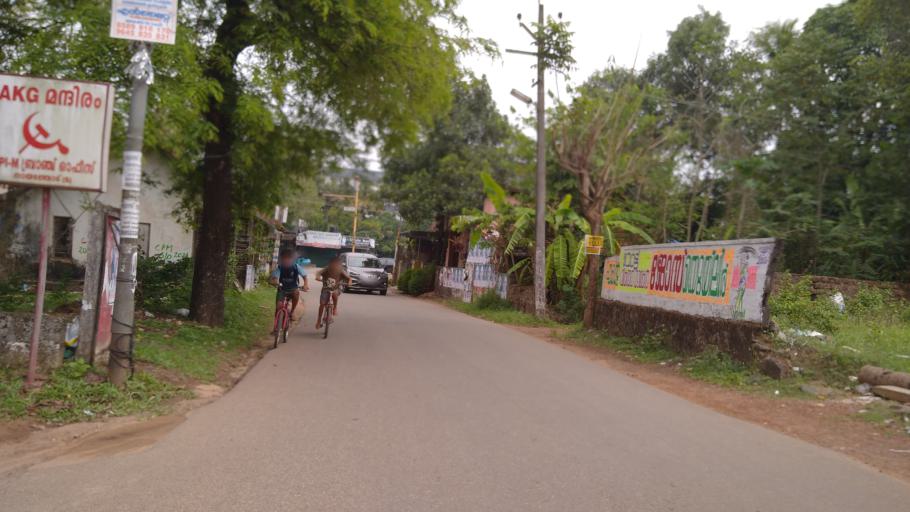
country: IN
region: Kerala
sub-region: Ernakulam
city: Angamali
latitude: 10.1626
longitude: 76.3964
